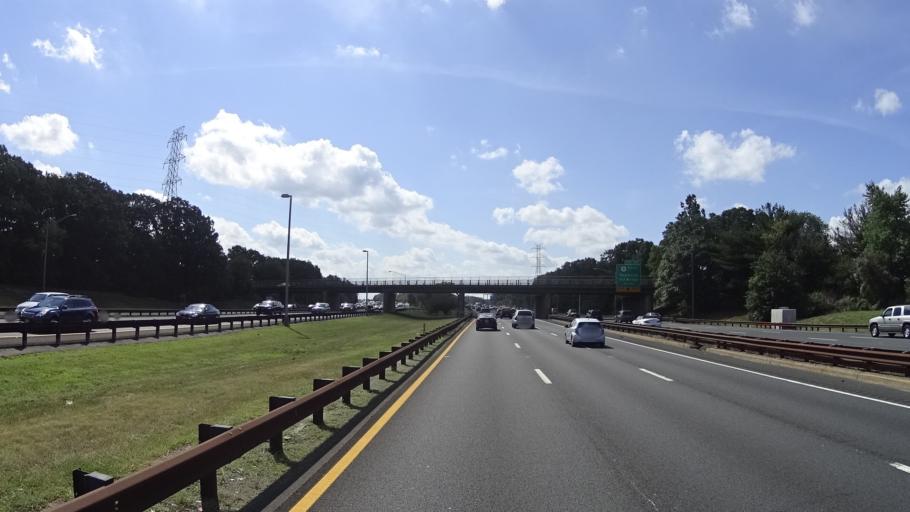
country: US
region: New Jersey
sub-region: Middlesex County
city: South Amboy
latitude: 40.4777
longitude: -74.3002
